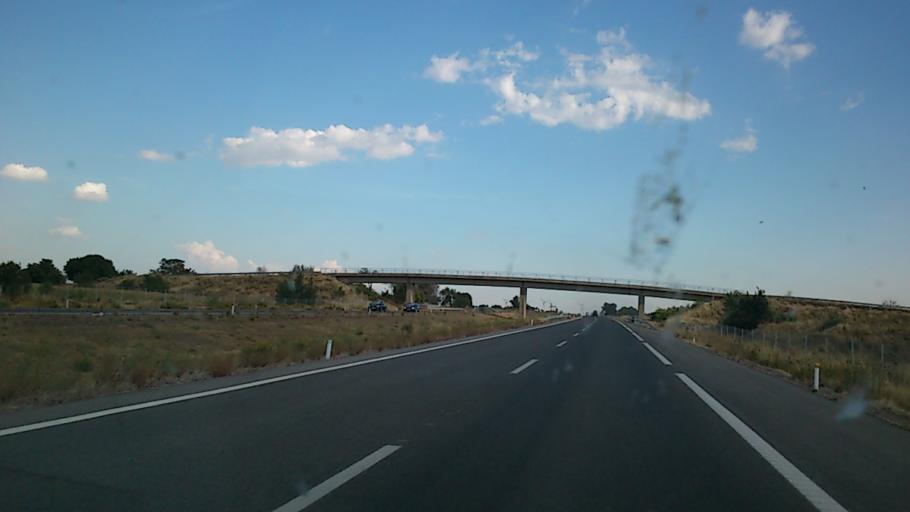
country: ES
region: Aragon
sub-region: Provincia de Zaragoza
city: Frescano
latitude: 41.9147
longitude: -1.4713
